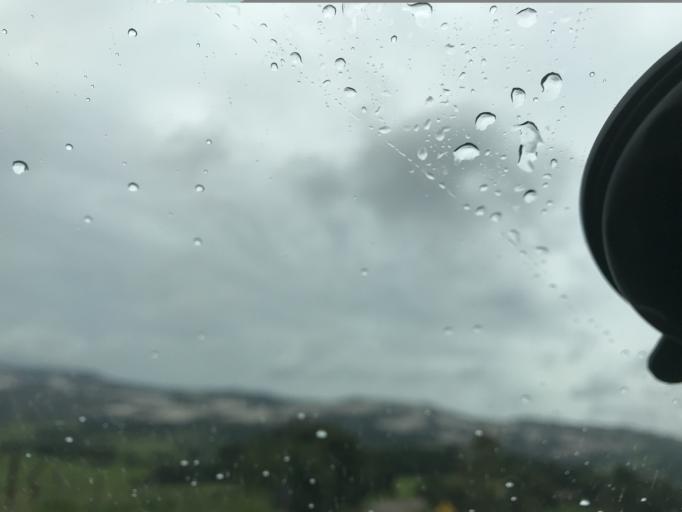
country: BR
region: Minas Gerais
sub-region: Conceicao Do Rio Verde
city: Conceicao do Rio Verde
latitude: -21.6916
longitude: -45.0065
